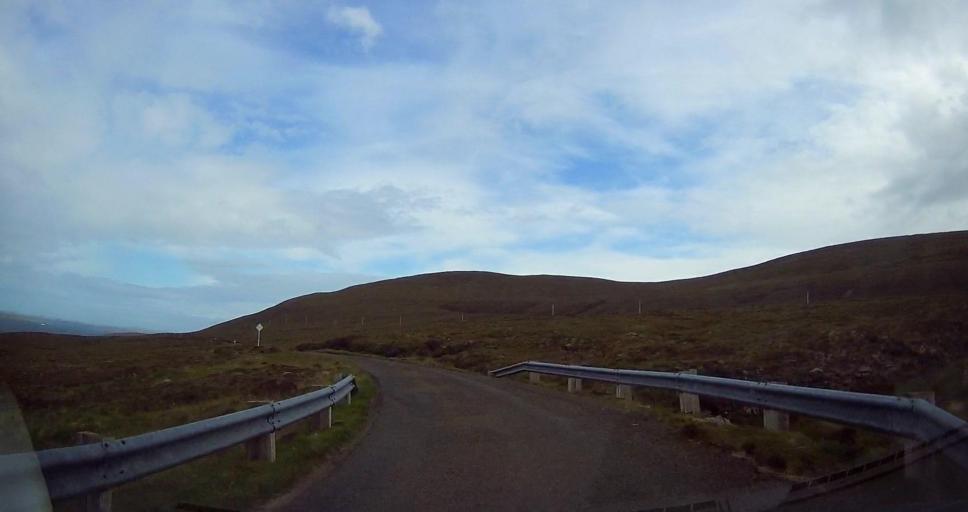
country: GB
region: Scotland
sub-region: Orkney Islands
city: Stromness
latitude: 58.8967
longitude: -3.2731
